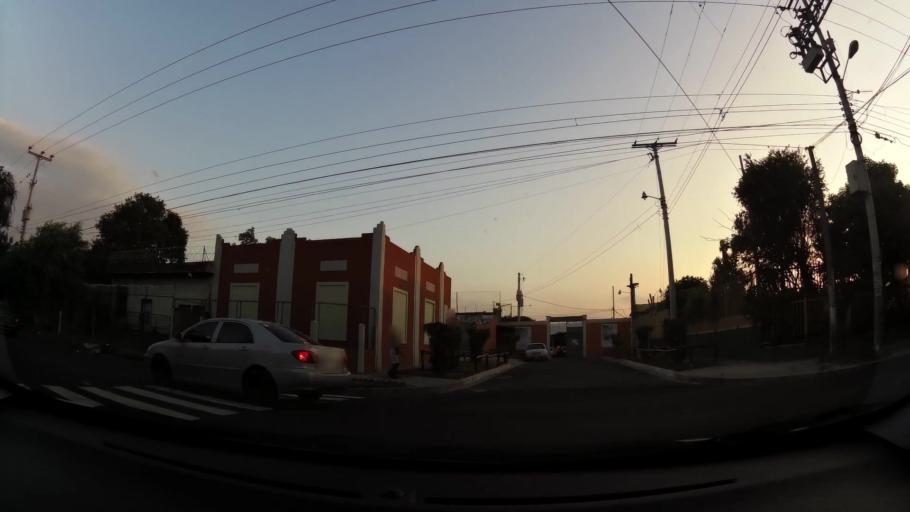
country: SV
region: San Salvador
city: San Salvador
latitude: 13.7097
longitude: -89.1878
